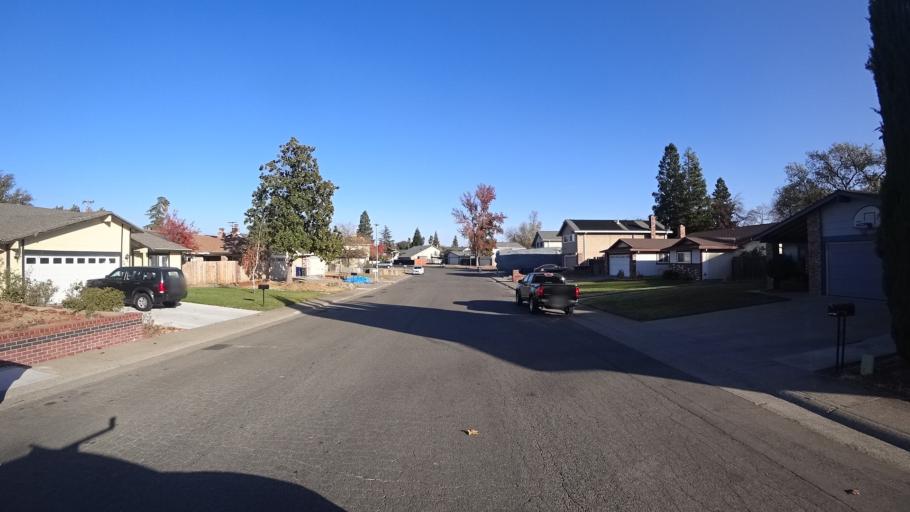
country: US
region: California
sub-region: Sacramento County
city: Antelope
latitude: 38.7015
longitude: -121.3080
